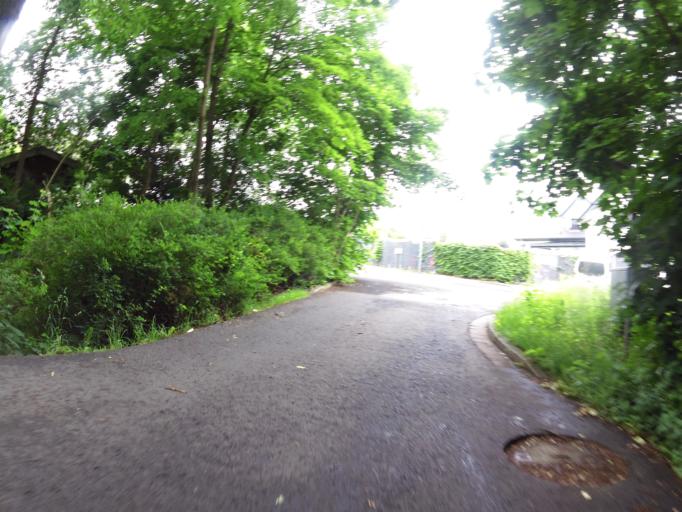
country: DE
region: Hesse
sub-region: Regierungsbezirk Kassel
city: Bad Hersfeld
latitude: 50.8671
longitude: 9.6937
